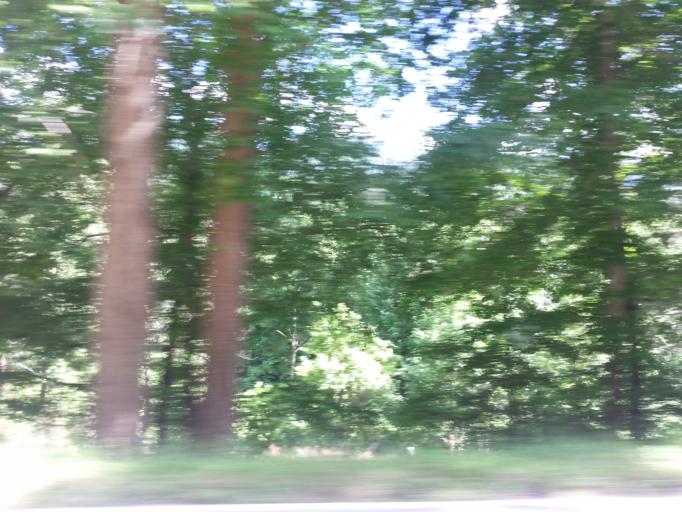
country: US
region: Kentucky
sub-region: Harlan County
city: Cumberland
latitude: 36.9444
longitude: -83.1248
